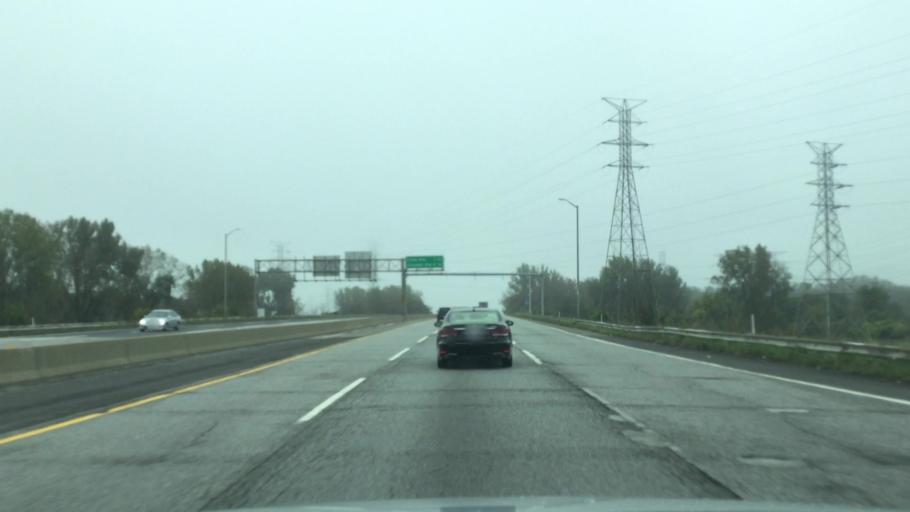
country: US
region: Indiana
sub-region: Lake County
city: Whiting
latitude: 41.6853
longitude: -87.5222
